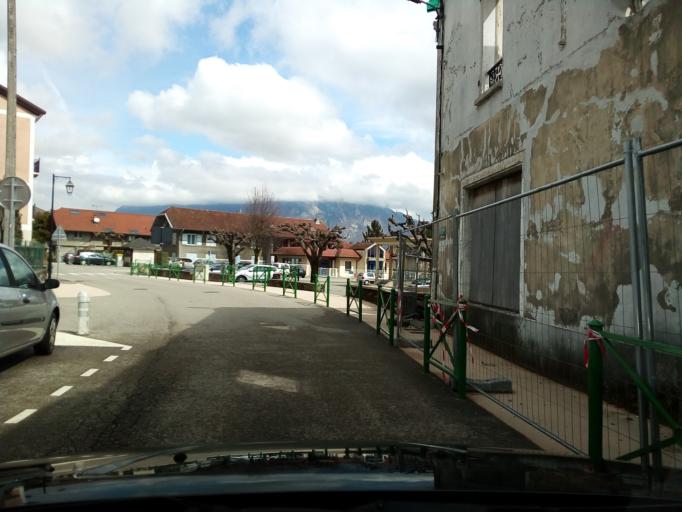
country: FR
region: Rhone-Alpes
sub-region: Departement de l'Isere
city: Chapareillan
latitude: 45.4628
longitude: 5.9903
